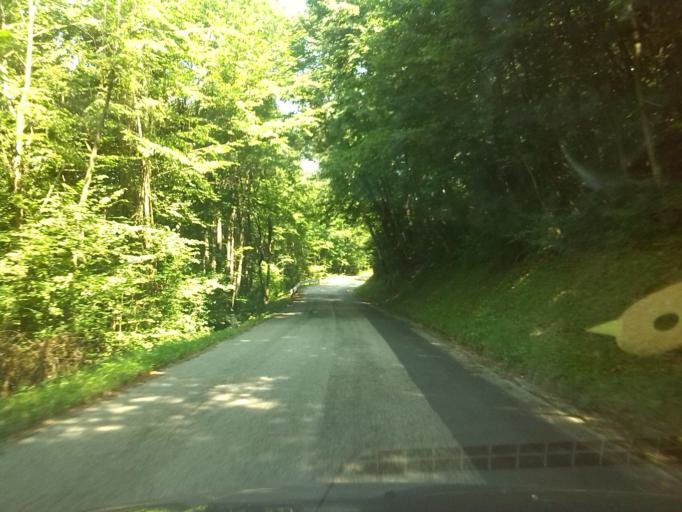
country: IT
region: Friuli Venezia Giulia
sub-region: Provincia di Udine
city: Stregna
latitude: 46.1273
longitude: 13.6051
